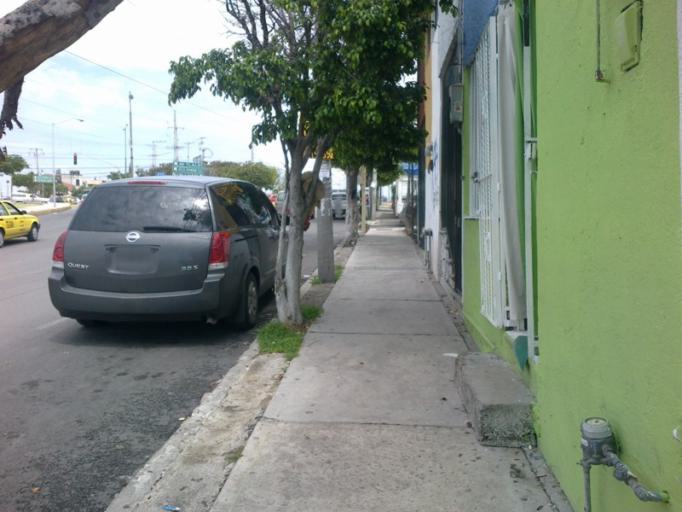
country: MX
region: Queretaro
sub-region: Queretaro
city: Sergio Villasenor
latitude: 20.6281
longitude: -100.4056
